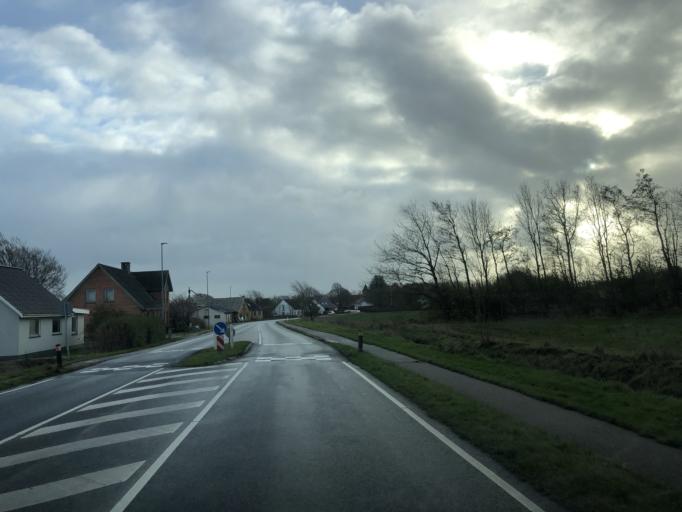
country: DK
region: North Denmark
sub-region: Rebild Kommune
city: Stovring
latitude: 56.8935
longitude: 9.7818
